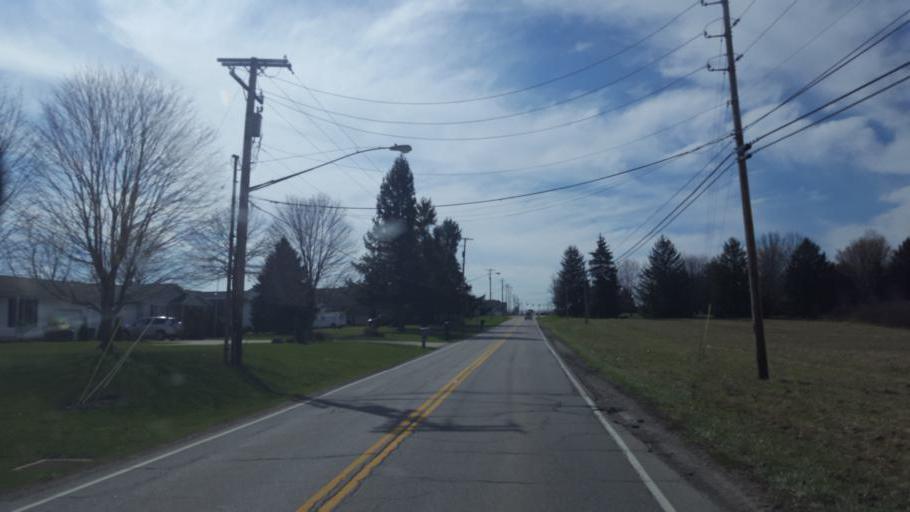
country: US
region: Ohio
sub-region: Richland County
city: Ontario
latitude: 40.7873
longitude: -82.5820
